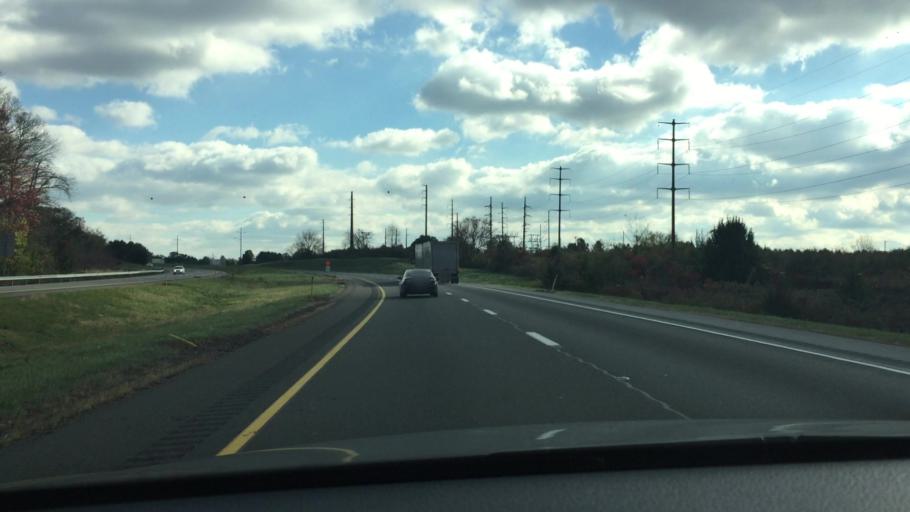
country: US
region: Pennsylvania
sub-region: Columbia County
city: Light Street
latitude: 41.0247
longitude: -76.4139
